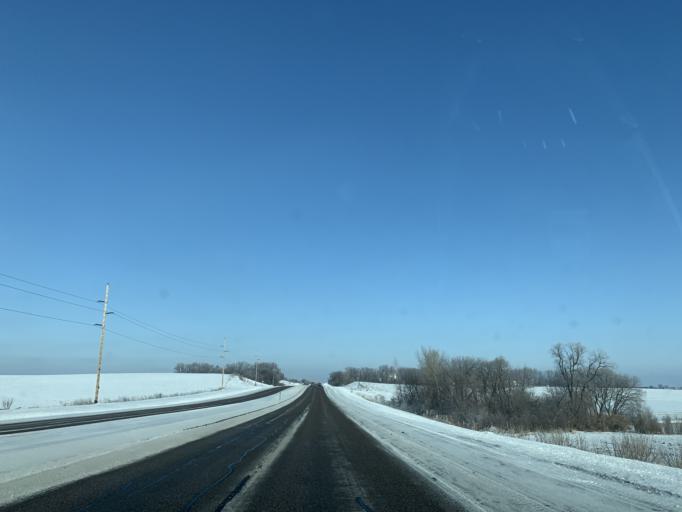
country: US
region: Minnesota
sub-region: Dakota County
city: Lakeville
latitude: 44.6634
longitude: -93.2174
